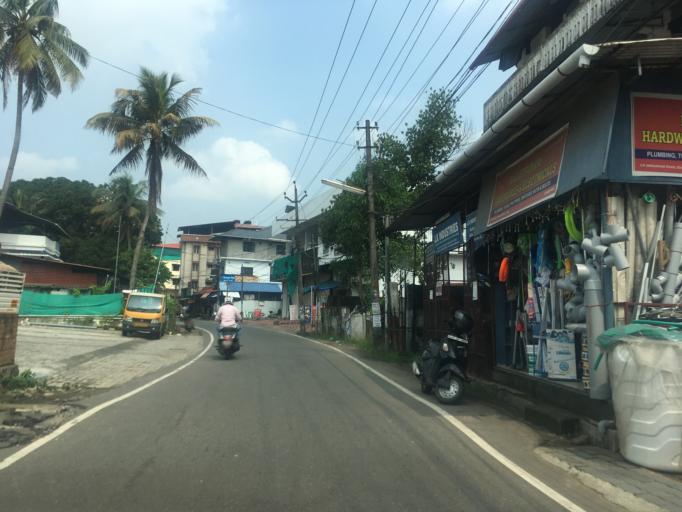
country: IN
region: Kerala
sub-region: Ernakulam
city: Elur
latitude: 10.0322
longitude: 76.3097
